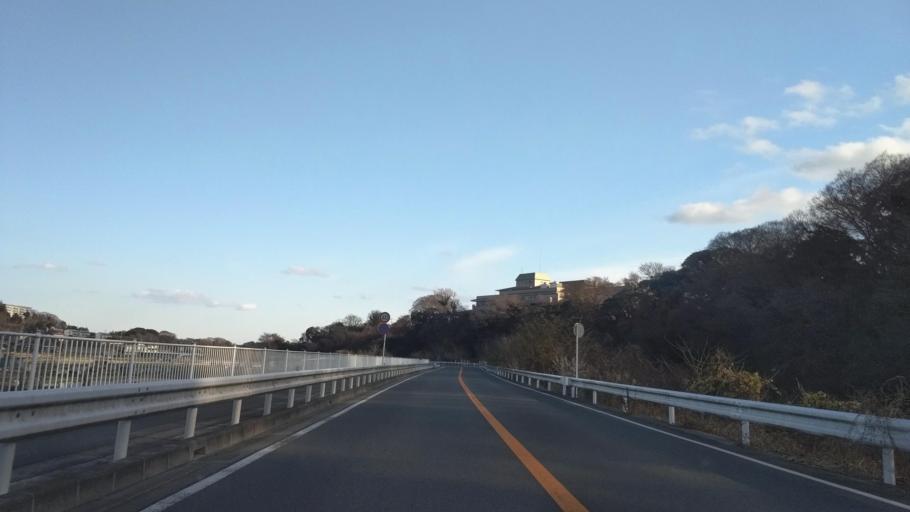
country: JP
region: Kanagawa
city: Hadano
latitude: 35.3578
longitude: 139.2546
